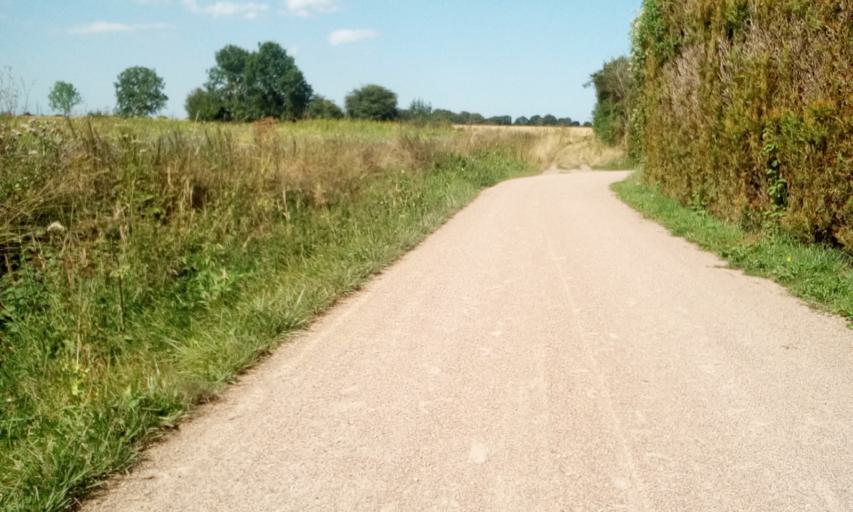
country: FR
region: Lower Normandy
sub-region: Departement du Calvados
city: Argences
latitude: 49.1339
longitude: -0.1146
